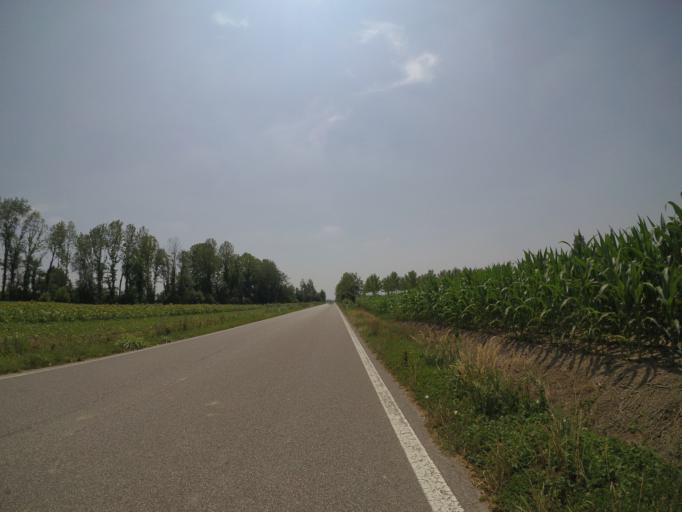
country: IT
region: Friuli Venezia Giulia
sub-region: Provincia di Udine
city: Rivignano
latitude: 45.8523
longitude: 13.0267
